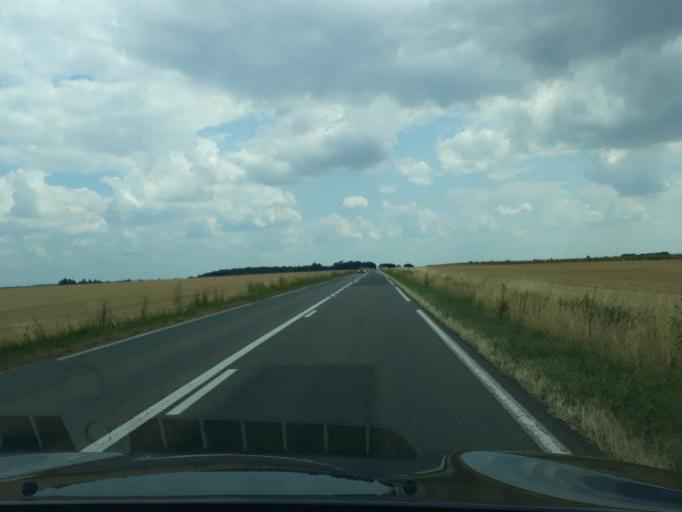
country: FR
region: Centre
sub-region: Departement du Cher
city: Avord
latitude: 47.0286
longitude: 2.6599
